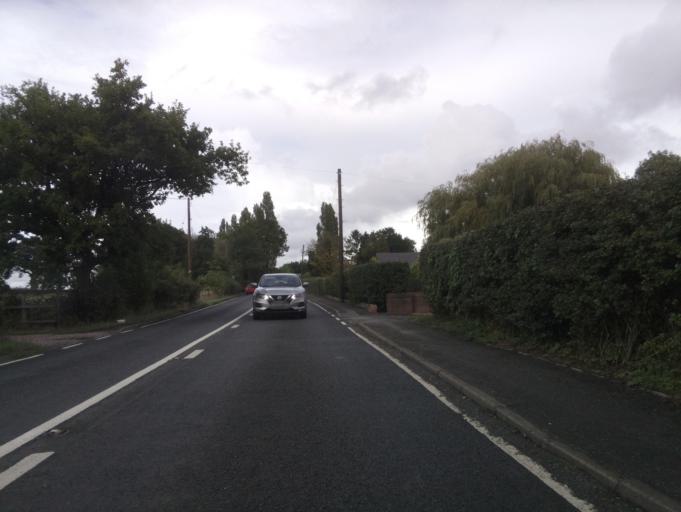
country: GB
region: England
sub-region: Worcestershire
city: Droitwich
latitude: 52.3191
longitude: -2.1761
